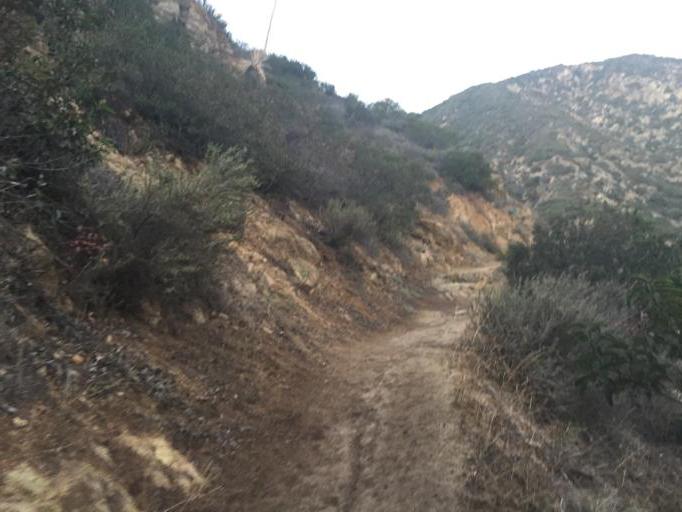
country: US
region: California
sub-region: Los Angeles County
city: Sierra Madre
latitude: 34.1786
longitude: -118.0459
